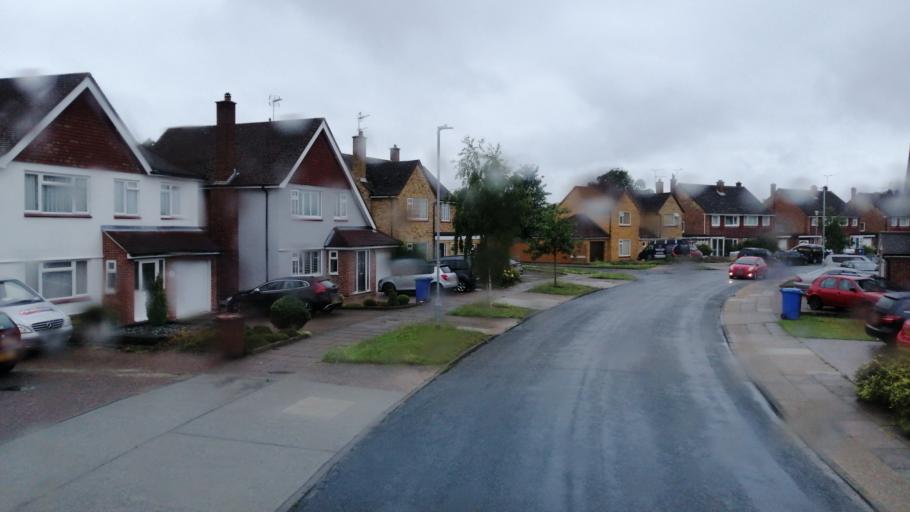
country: GB
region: England
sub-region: Suffolk
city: Kesgrave
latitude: 52.0487
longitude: 1.2046
